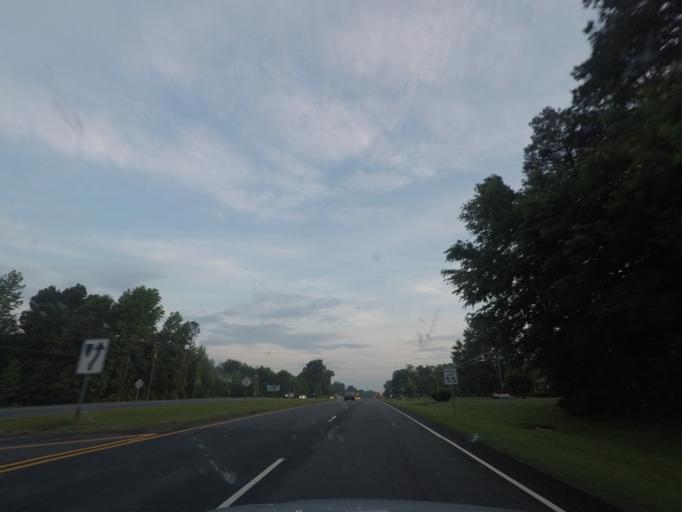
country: US
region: North Carolina
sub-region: Person County
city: Roxboro
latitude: 36.2804
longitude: -78.9535
